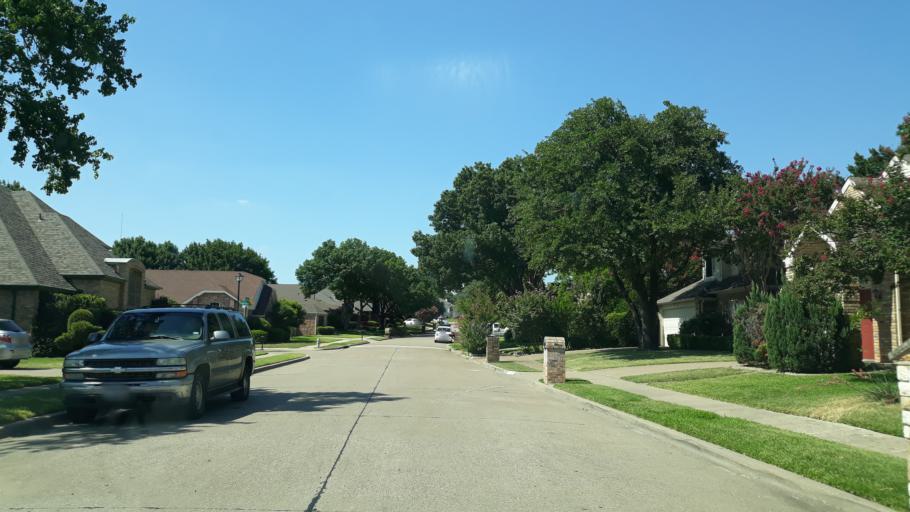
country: US
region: Texas
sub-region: Dallas County
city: Irving
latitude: 32.8249
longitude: -97.0094
